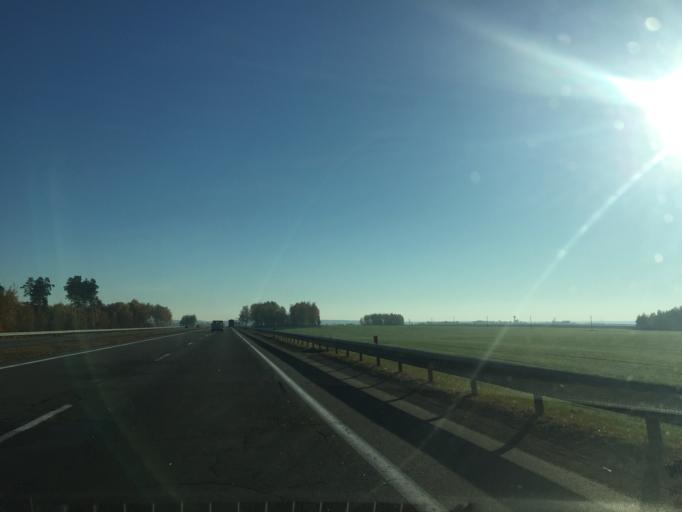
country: BY
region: Minsk
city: Smilavichy
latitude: 53.7639
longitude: 28.1215
